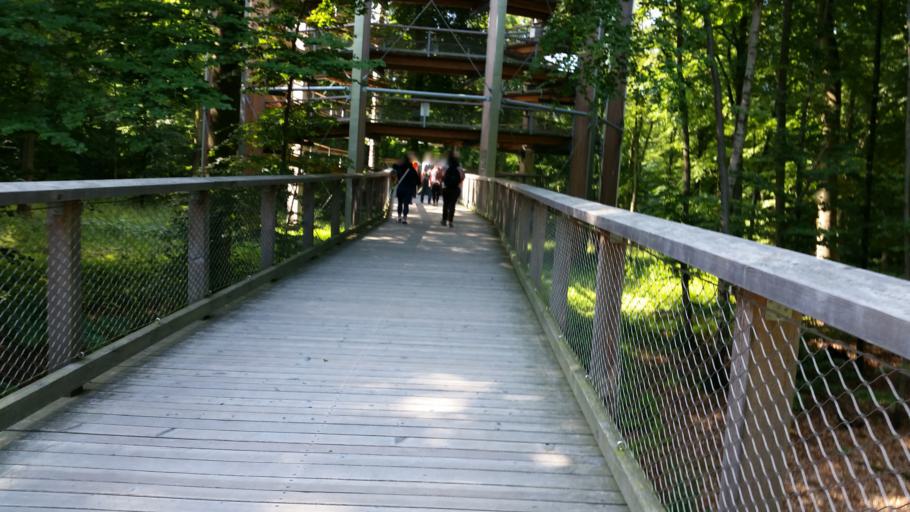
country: DE
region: Mecklenburg-Vorpommern
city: Ostseebad Binz
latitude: 54.4323
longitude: 13.5576
